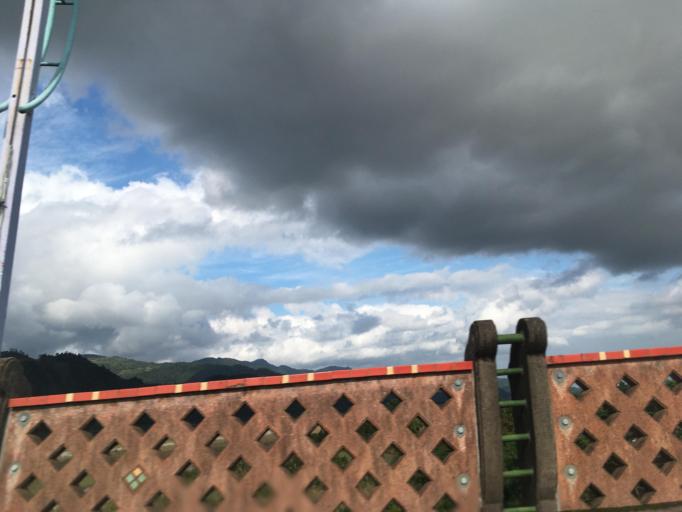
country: TW
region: Taiwan
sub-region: Yilan
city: Yilan
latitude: 24.6680
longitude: 121.6126
